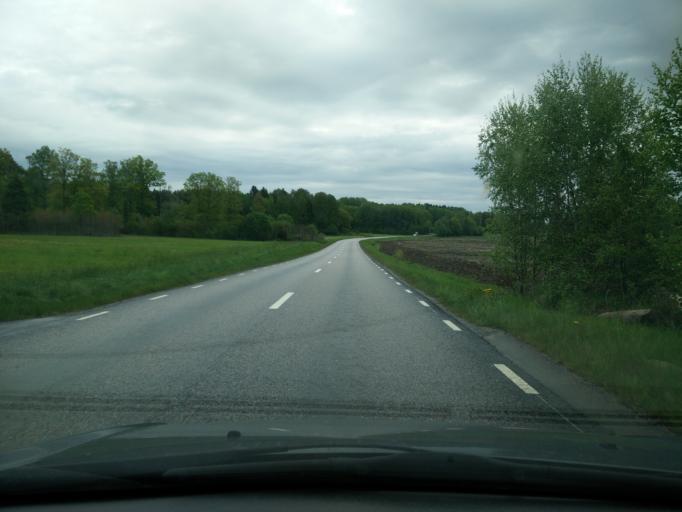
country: SE
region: Stockholm
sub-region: Norrtalje Kommun
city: Norrtalje
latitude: 59.7831
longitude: 18.7865
